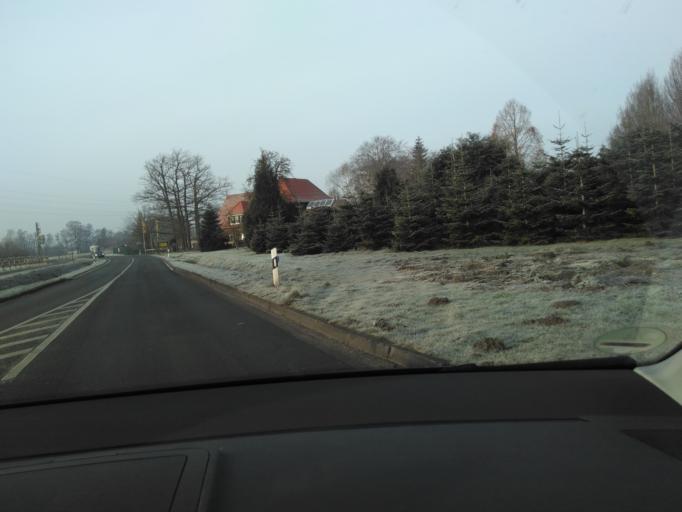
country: DE
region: North Rhine-Westphalia
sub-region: Regierungsbezirk Detmold
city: Verl
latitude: 51.8646
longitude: 8.4976
